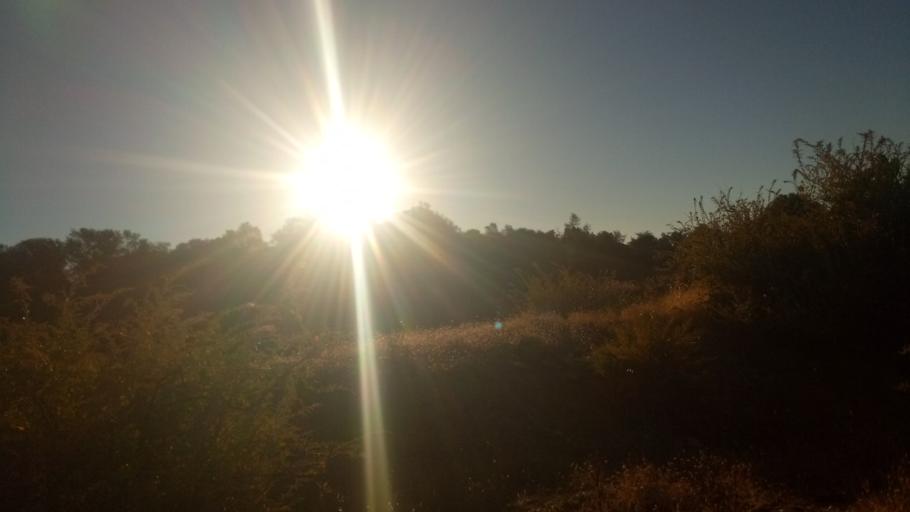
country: PT
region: Faro
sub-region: Tavira
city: Tavira
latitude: 37.1446
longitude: -7.6180
